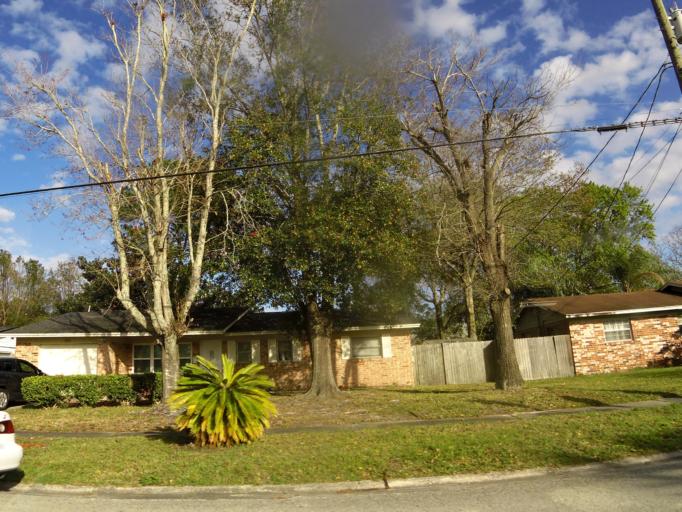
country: US
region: Florida
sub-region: Duval County
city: Jacksonville
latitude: 30.2848
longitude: -81.6065
